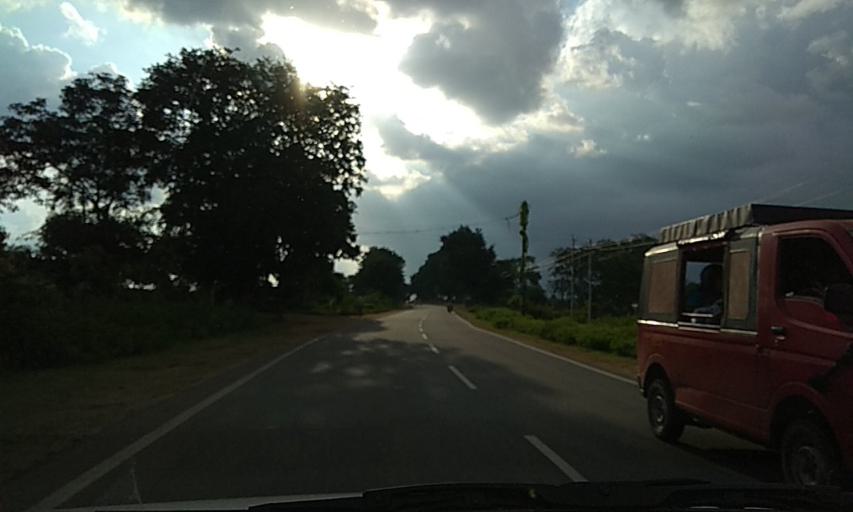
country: IN
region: Karnataka
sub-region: Chamrajnagar
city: Gundlupet
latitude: 11.8103
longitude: 76.7208
